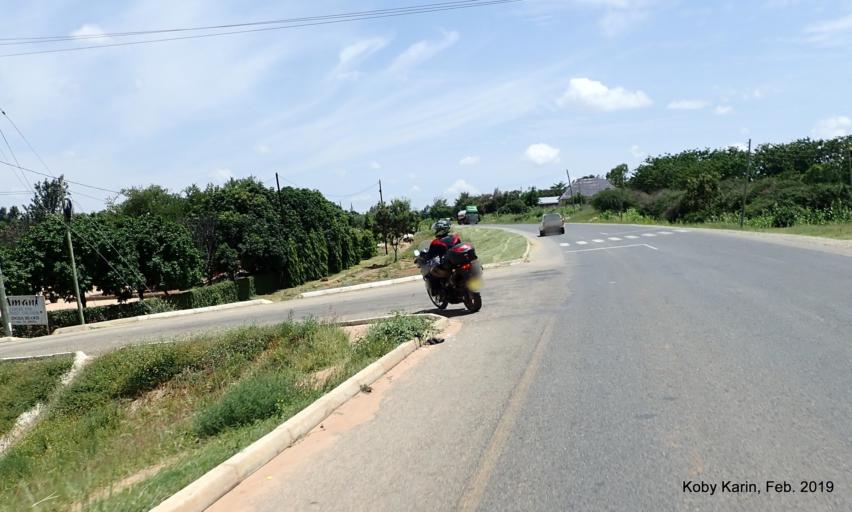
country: TZ
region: Singida
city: Singida
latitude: -4.7965
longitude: 34.7374
